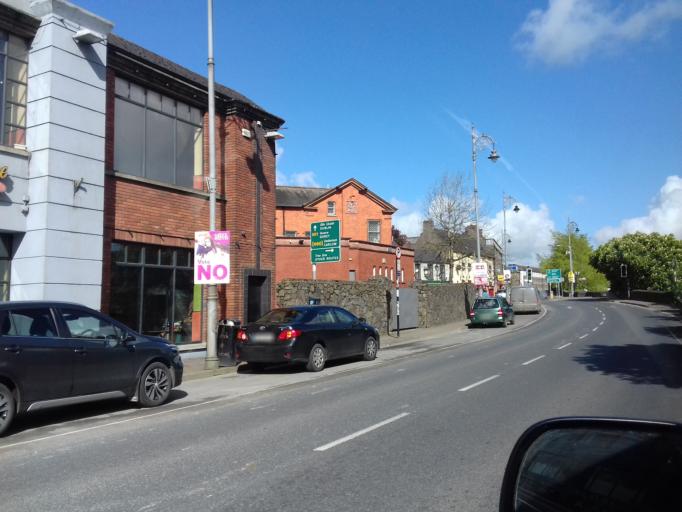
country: IE
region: Leinster
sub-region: Loch Garman
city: Enniscorthy
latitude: 52.5014
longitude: -6.5654
